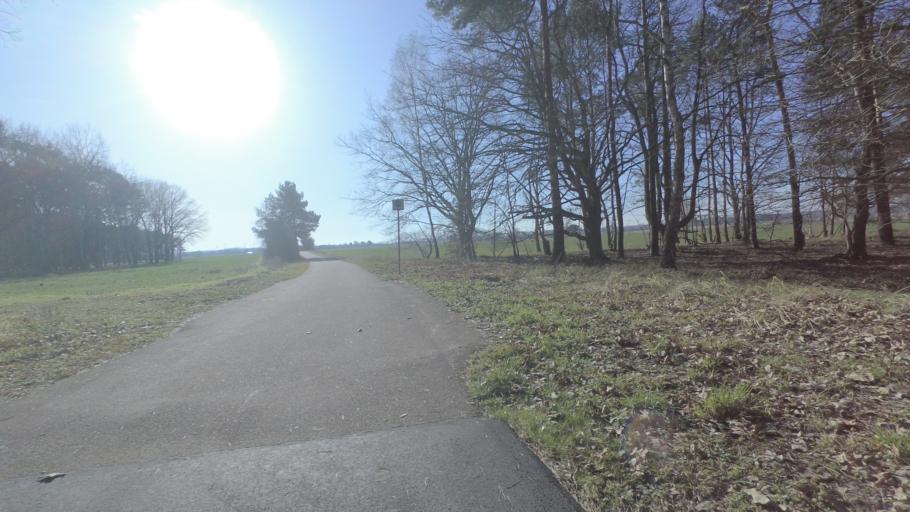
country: DE
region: Brandenburg
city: Juterbog
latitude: 52.0217
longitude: 13.1283
